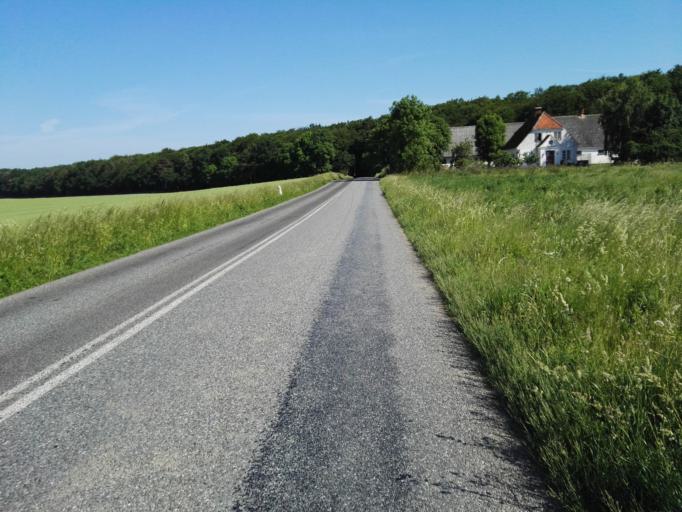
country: DK
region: Zealand
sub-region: Lejre Kommune
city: Ejby
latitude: 55.7276
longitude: 11.8875
